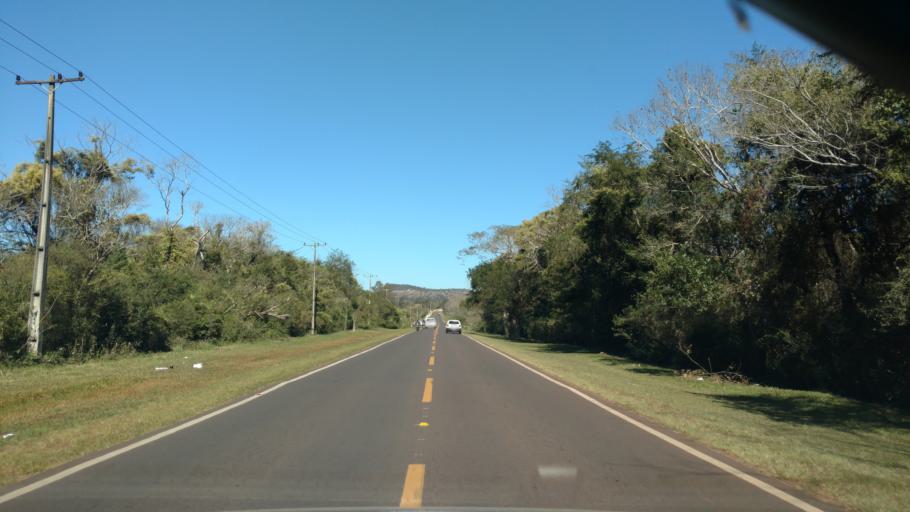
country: PY
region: Paraguari
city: Yaguaron
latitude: -25.5451
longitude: -57.2786
